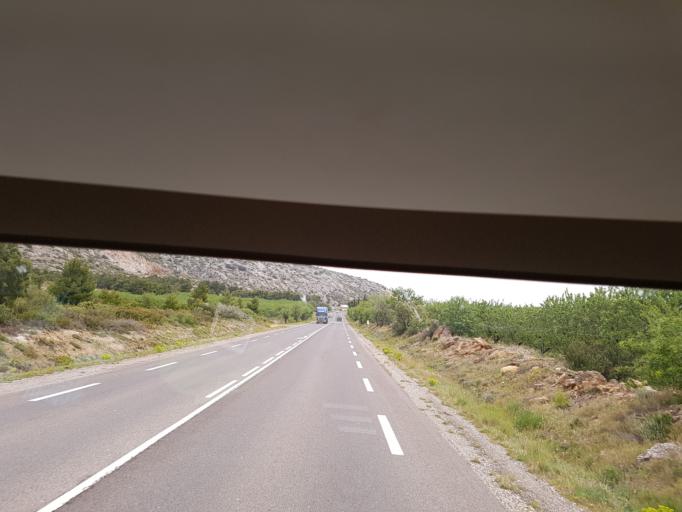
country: FR
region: Languedoc-Roussillon
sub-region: Departement des Pyrenees-Orientales
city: Salses-le-Chateau
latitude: 42.8556
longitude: 2.9503
